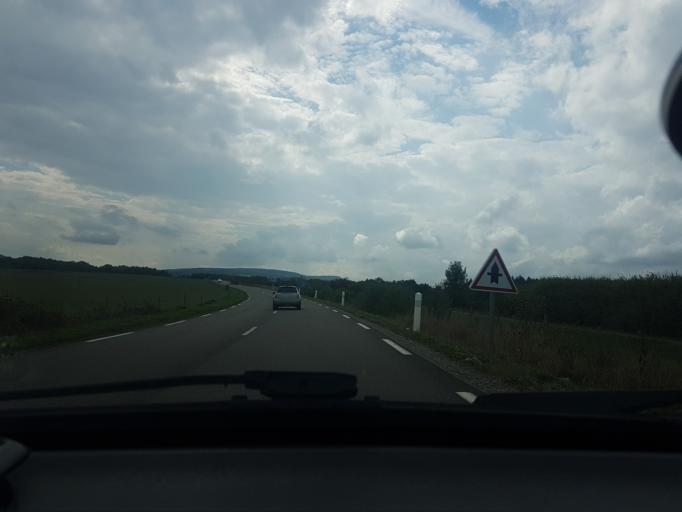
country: FR
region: Franche-Comte
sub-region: Departement du Doubs
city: Arcey
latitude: 47.5768
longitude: 6.6579
